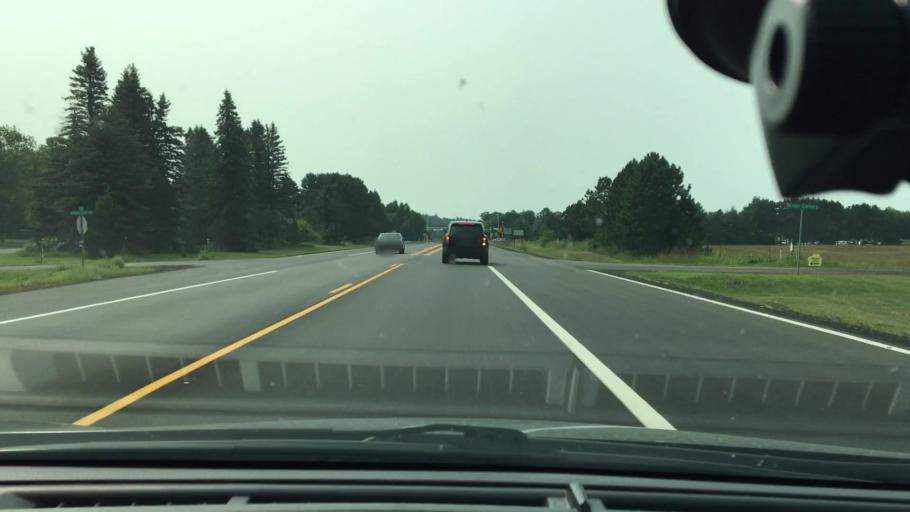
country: US
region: Minnesota
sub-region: Crow Wing County
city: Brainerd
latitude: 46.4022
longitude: -94.1764
